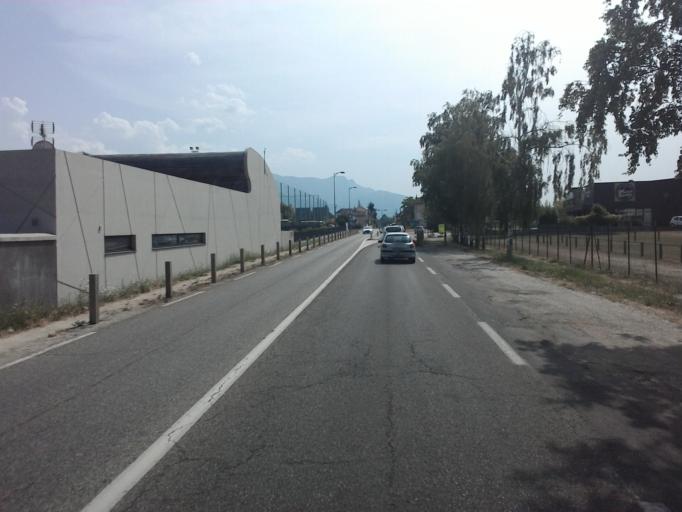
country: FR
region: Rhone-Alpes
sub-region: Departement de l'Isere
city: Voiron
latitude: 45.3547
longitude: 5.5983
